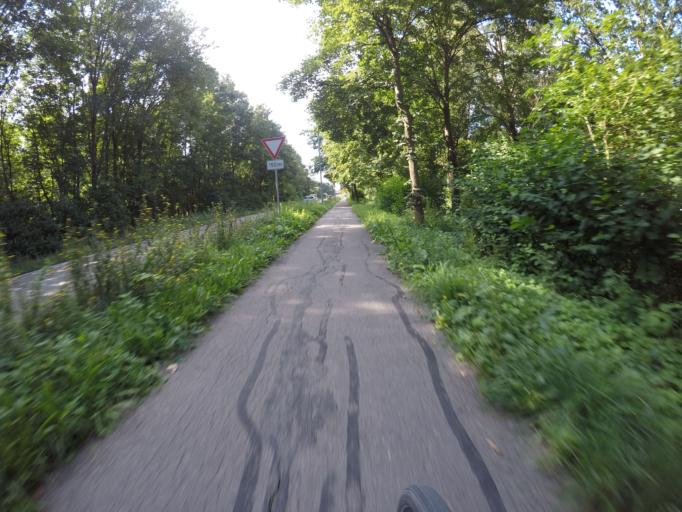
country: DE
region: Baden-Wuerttemberg
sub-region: Regierungsbezirk Stuttgart
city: Wendlingen am Neckar
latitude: 48.6717
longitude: 9.3674
